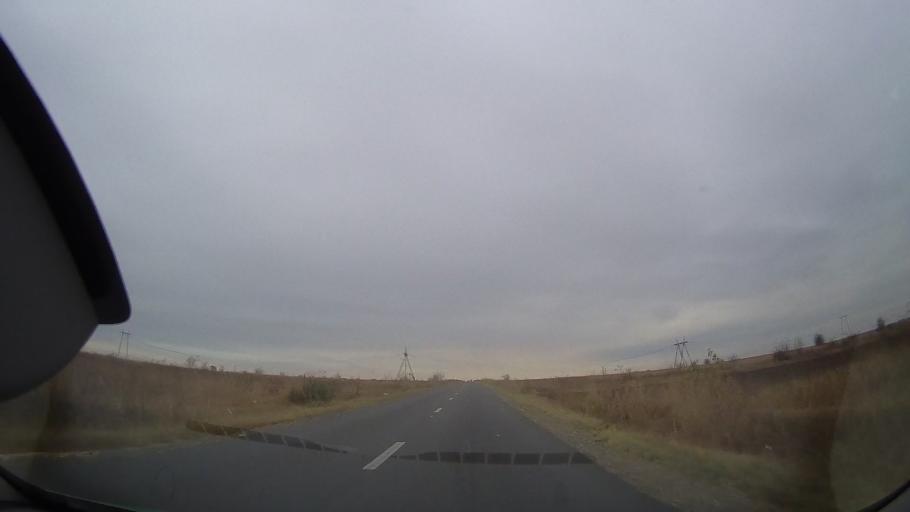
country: RO
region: Ialomita
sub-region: Oras Amara
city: Amara
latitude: 44.6368
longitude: 27.3008
